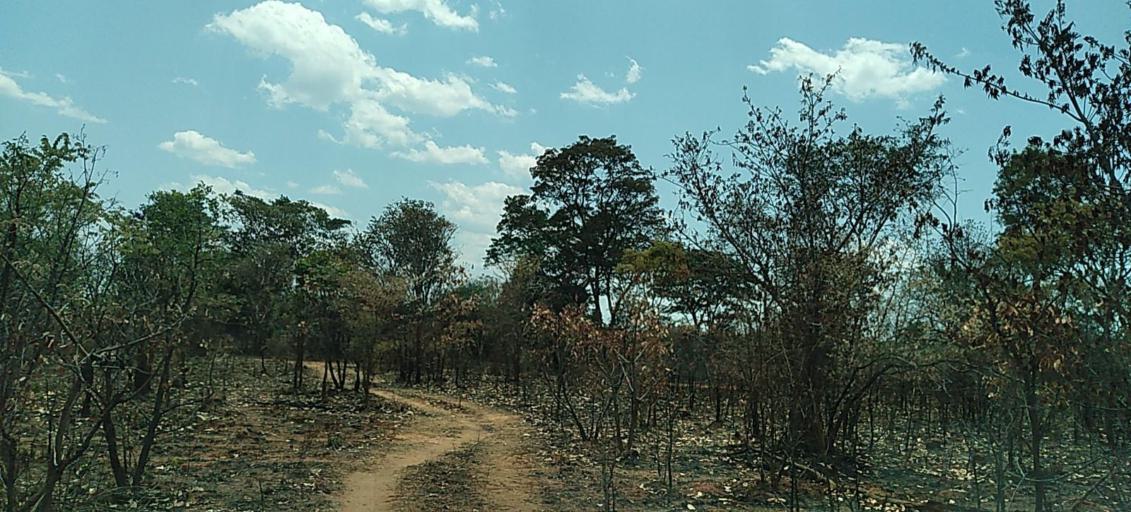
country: ZM
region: Central
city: Kapiri Mposhi
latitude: -13.6300
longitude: 28.7728
